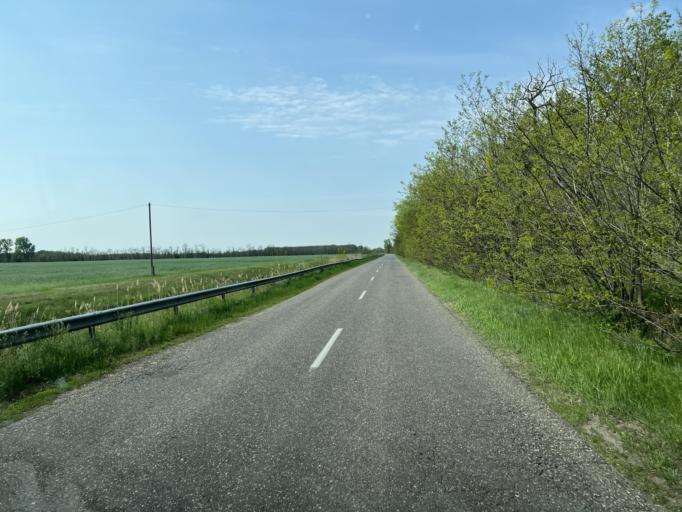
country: HU
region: Pest
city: Tortel
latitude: 47.1103
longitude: 19.9138
